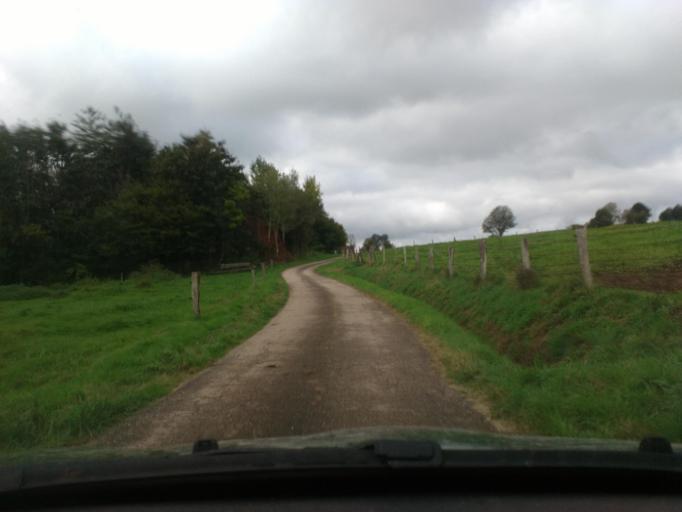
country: FR
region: Lorraine
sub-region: Departement des Vosges
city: Etival-Clairefontaine
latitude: 48.3347
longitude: 6.8620
